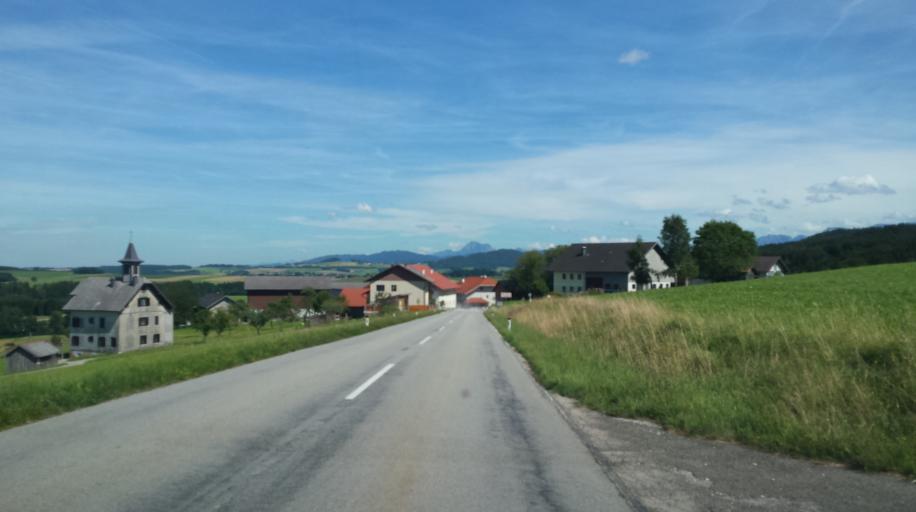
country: AT
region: Upper Austria
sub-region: Politischer Bezirk Vocklabruck
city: Frankenmarkt
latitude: 47.9515
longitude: 13.4184
